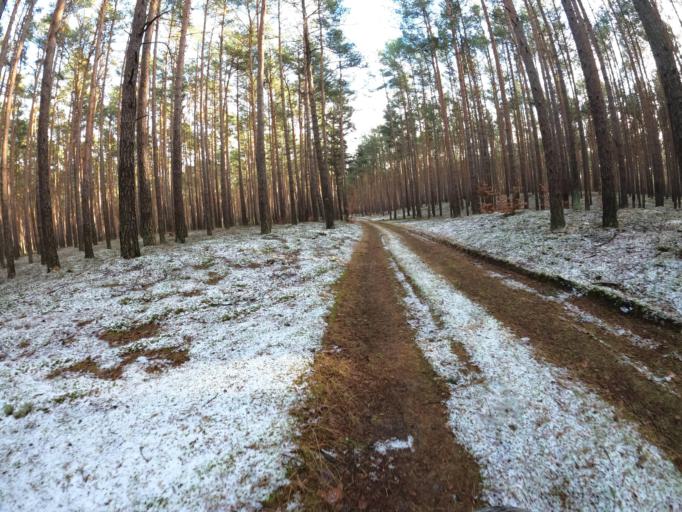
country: PL
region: Lubusz
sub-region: Powiat slubicki
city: Cybinka
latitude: 52.2337
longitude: 14.8293
